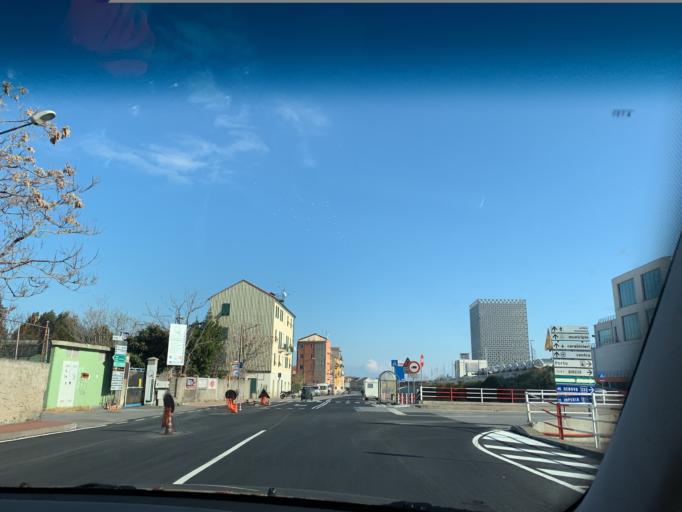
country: IT
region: Liguria
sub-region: Provincia di Savona
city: Vado Centro
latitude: 44.2667
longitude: 8.4300
